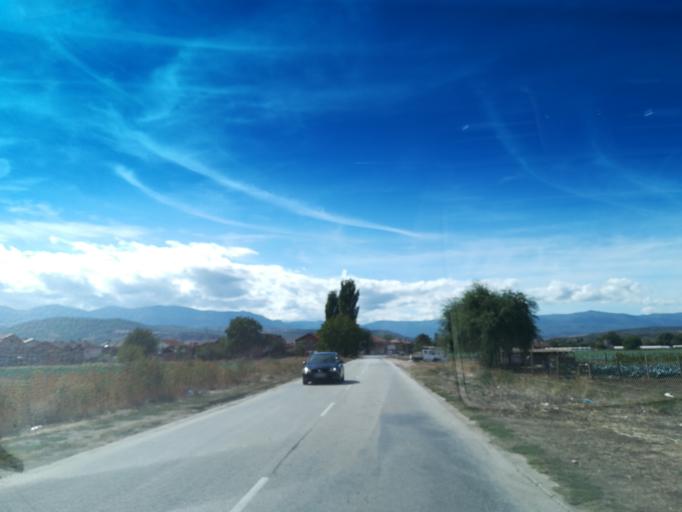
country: BG
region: Plovdiv
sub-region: Obshtina Krichim
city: Krichim
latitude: 42.0876
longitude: 24.4391
